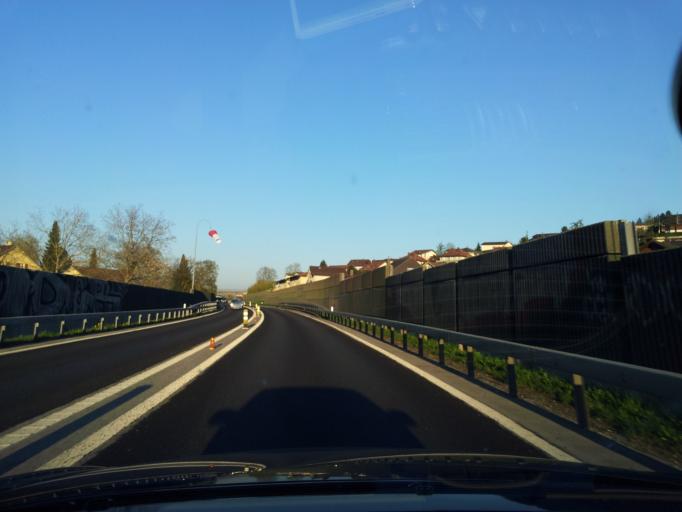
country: CH
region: Bern
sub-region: Biel/Bienne District
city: Brugg
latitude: 47.1178
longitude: 7.2851
